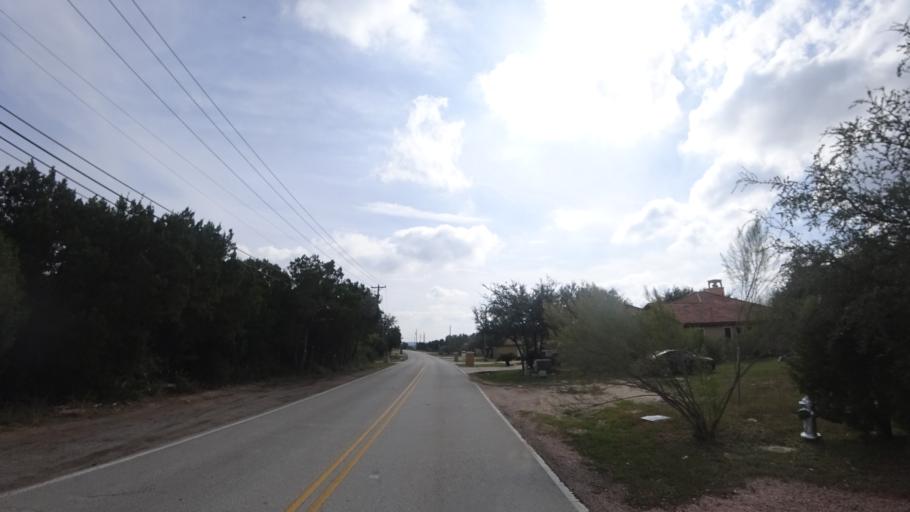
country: US
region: Texas
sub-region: Travis County
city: Hudson Bend
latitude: 30.3887
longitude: -97.9297
